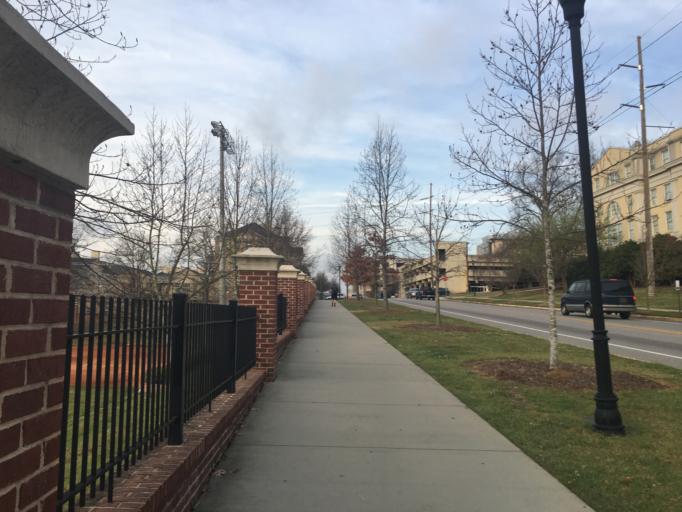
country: US
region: South Carolina
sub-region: Richland County
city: Columbia
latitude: 33.9926
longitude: -81.0268
